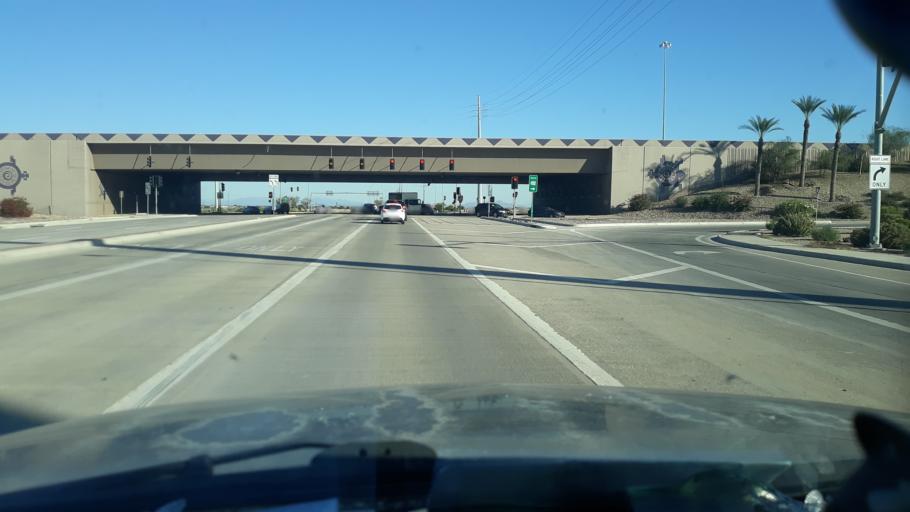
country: US
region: Arizona
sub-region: Maricopa County
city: Citrus Park
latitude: 33.5952
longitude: -112.4194
